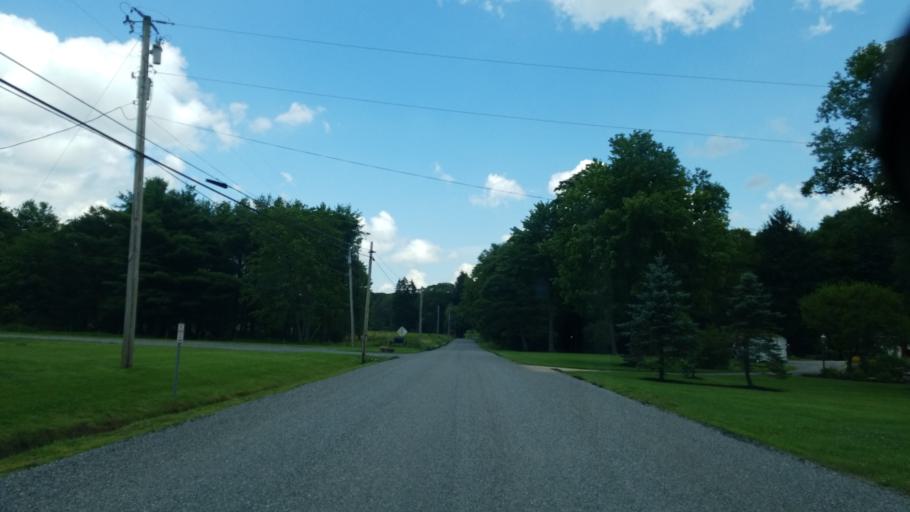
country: US
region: Pennsylvania
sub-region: Jefferson County
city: Brookville
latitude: 41.2307
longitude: -78.9983
